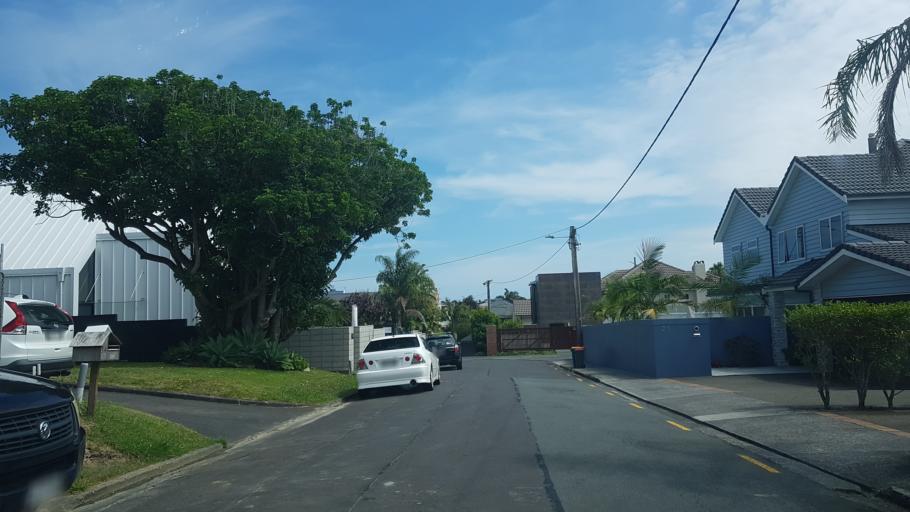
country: NZ
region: Auckland
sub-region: Auckland
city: North Shore
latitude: -36.7924
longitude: 174.7782
